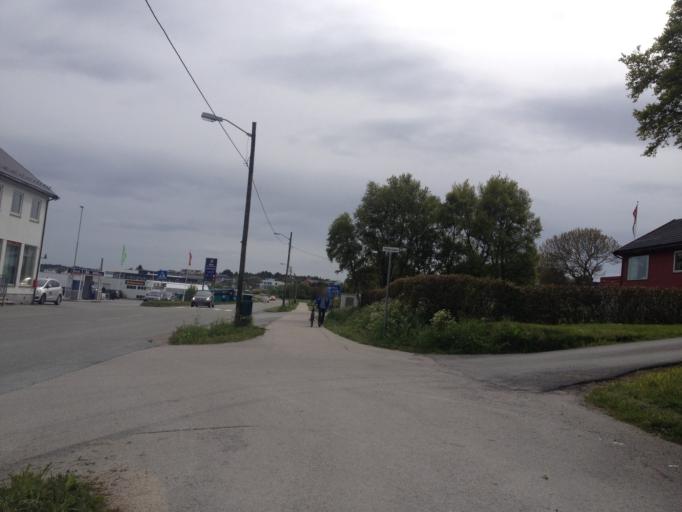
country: NO
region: Sor-Trondelag
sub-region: Froya
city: Sistranda
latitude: 63.7361
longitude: 8.8330
